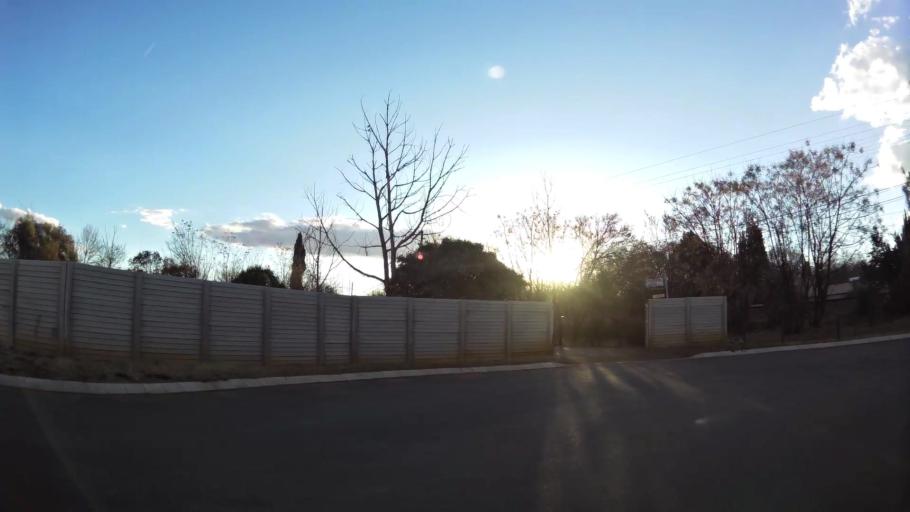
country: ZA
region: North-West
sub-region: Dr Kenneth Kaunda District Municipality
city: Potchefstroom
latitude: -26.6790
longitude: 27.1014
